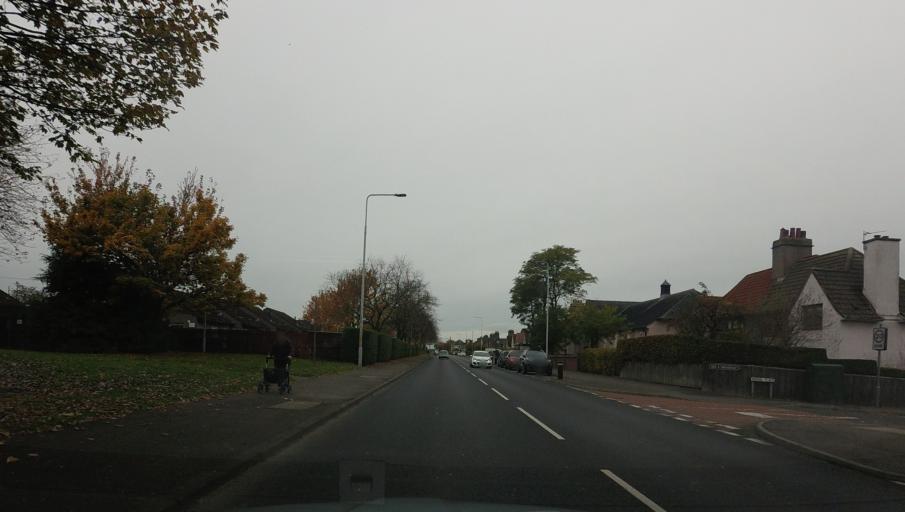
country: GB
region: Scotland
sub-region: Fife
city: Rosyth
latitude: 56.0362
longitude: -3.4198
